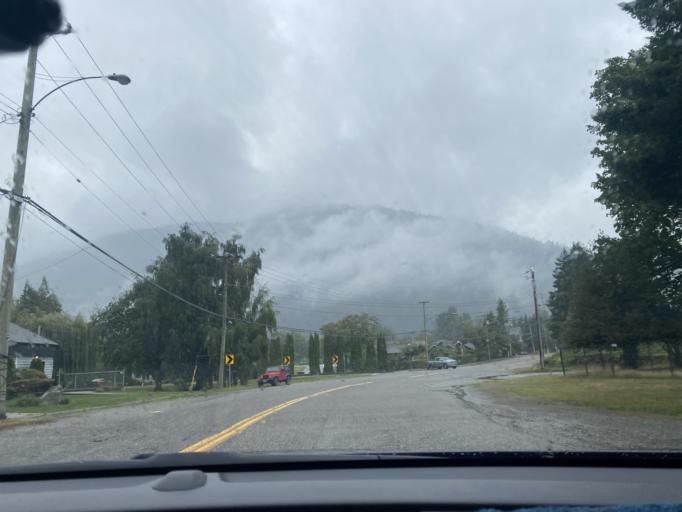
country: CA
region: British Columbia
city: Agassiz
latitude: 49.3027
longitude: -121.7760
